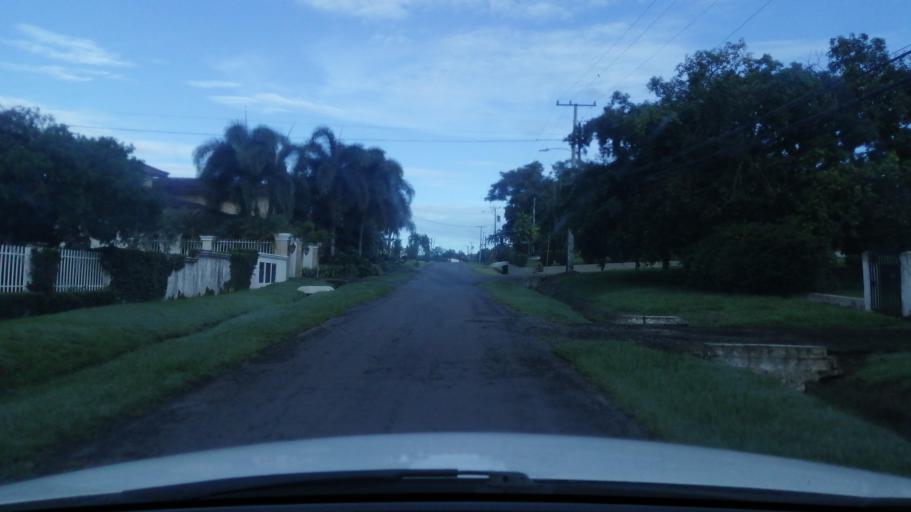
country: PA
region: Chiriqui
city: Mata del Nance
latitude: 8.4580
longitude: -82.4150
